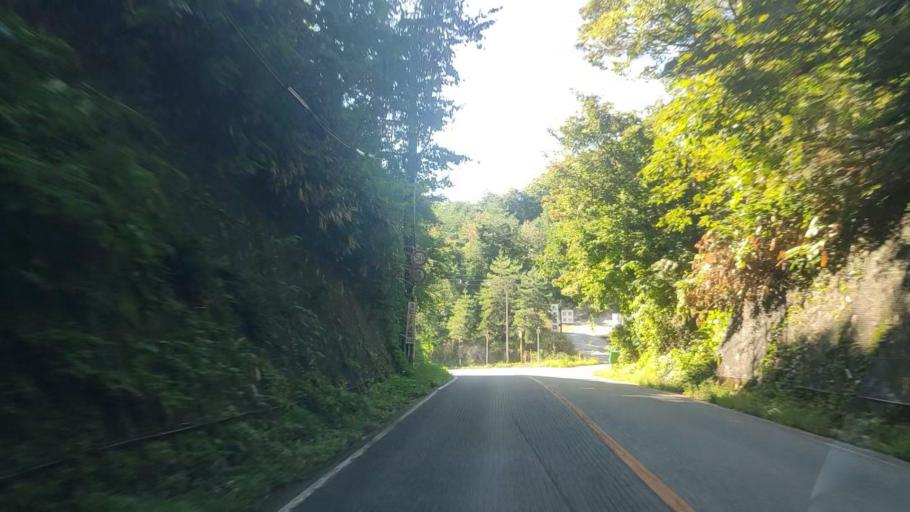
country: JP
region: Ishikawa
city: Nanao
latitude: 37.3213
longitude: 137.1692
